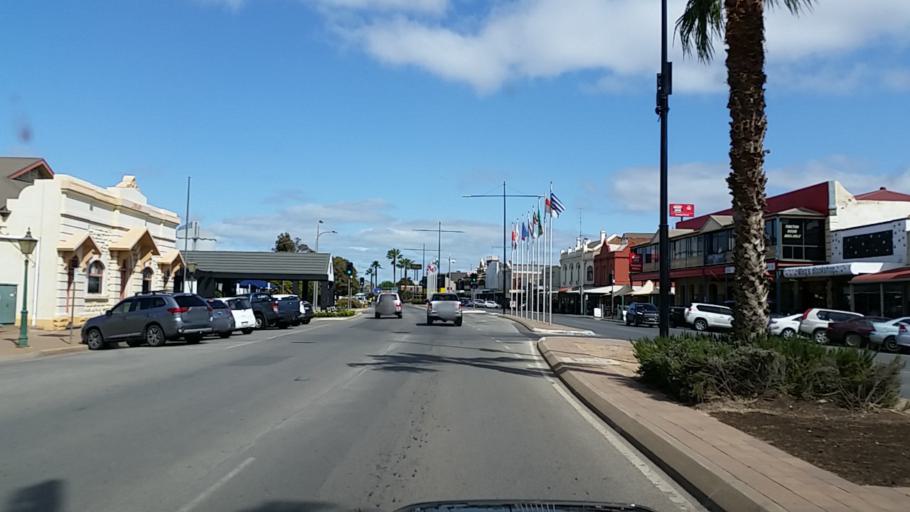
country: AU
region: South Australia
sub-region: Port Pirie City and Dists
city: Port Pirie
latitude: -33.1762
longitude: 138.0102
